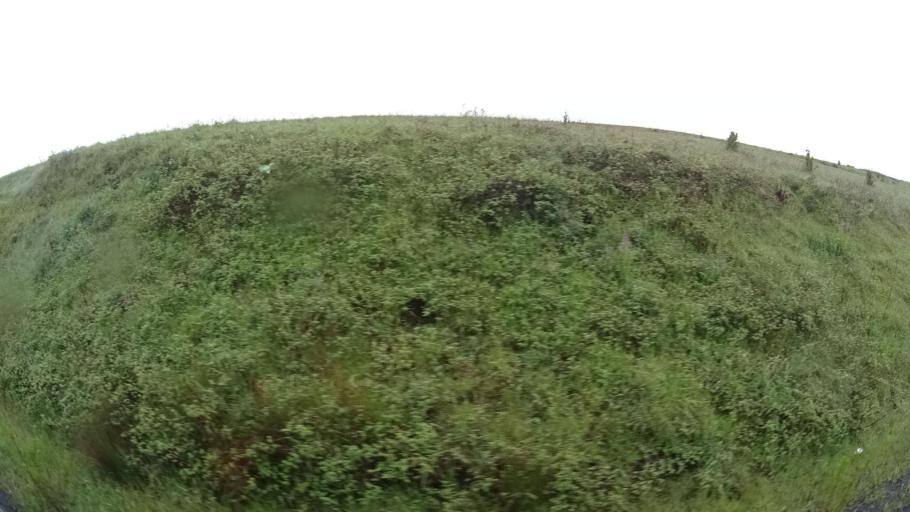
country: US
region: California
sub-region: Humboldt County
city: Westhaven-Moonstone
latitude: 41.1705
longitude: -123.9191
